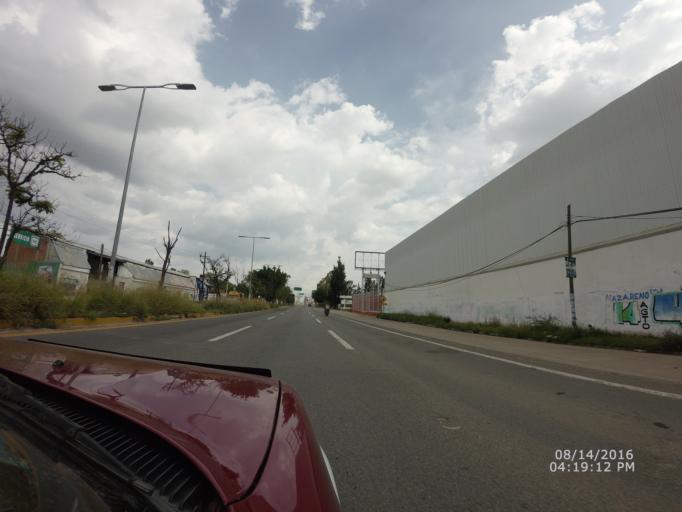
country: MX
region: Oaxaca
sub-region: San Lorenzo Cacaotepec
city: Santiago Etla
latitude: 17.1385
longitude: -96.7759
